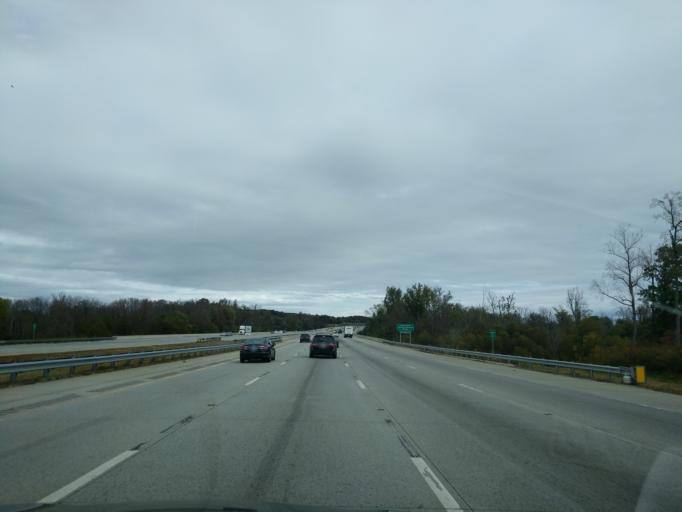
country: US
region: North Carolina
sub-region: Rowan County
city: Spencer
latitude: 35.7147
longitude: -80.3928
